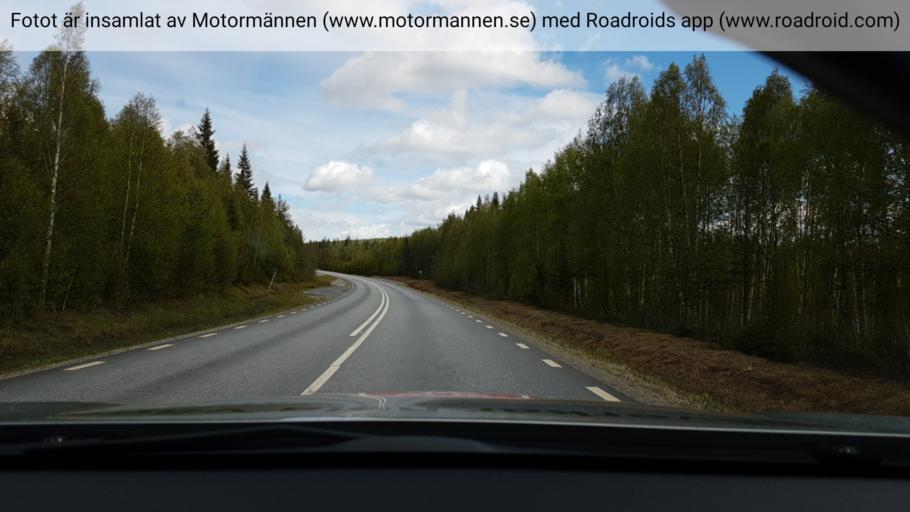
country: SE
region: Vaesterbotten
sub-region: Asele Kommun
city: Insjon
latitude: 64.1953
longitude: 17.6741
